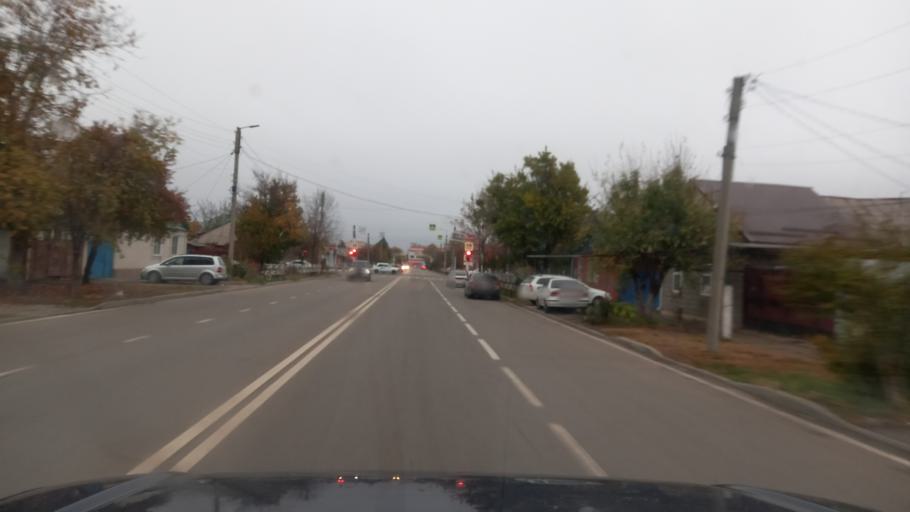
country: RU
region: Adygeya
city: Maykop
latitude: 44.6170
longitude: 40.1022
